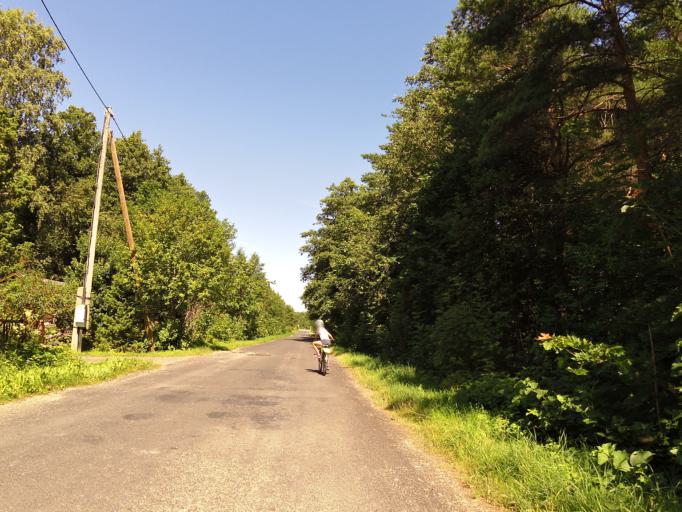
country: EE
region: Hiiumaa
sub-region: Kaerdla linn
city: Kardla
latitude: 58.7827
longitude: 22.4906
